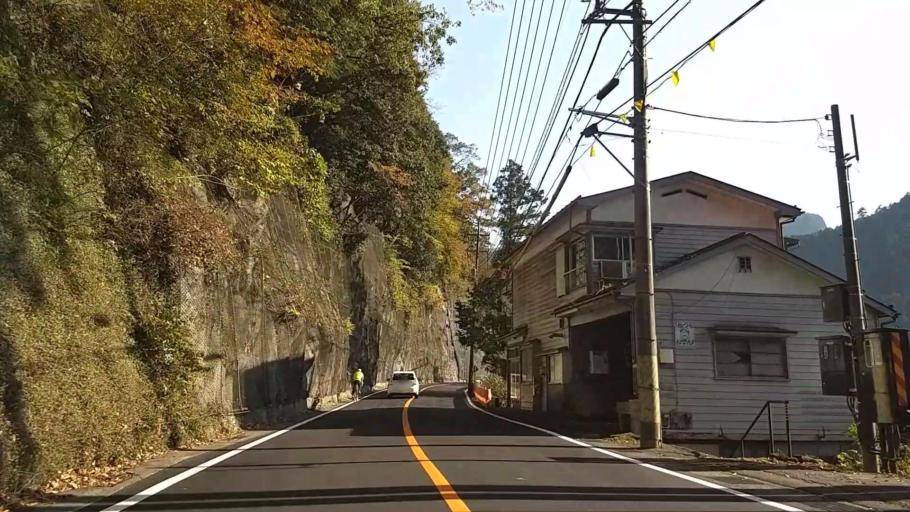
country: JP
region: Tokyo
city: Ome
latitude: 35.8153
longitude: 139.1318
